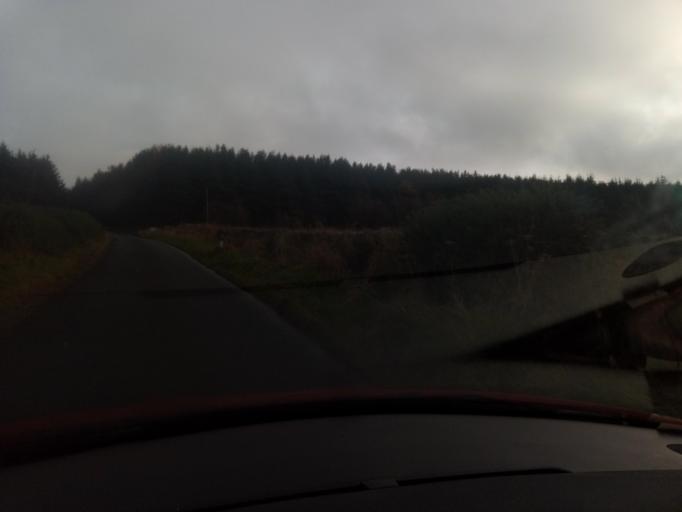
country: GB
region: Scotland
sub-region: The Scottish Borders
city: Jedburgh
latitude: 55.4859
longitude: -2.5923
